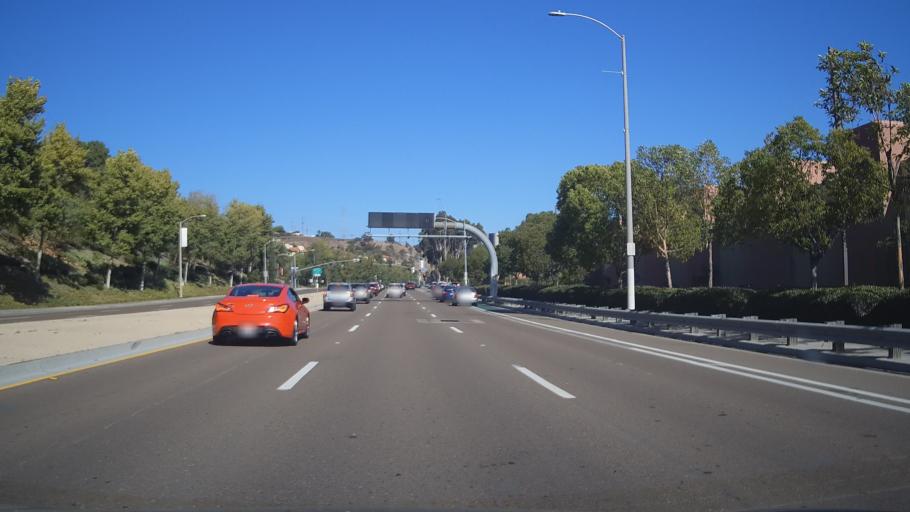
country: US
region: California
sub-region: San Diego County
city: San Diego
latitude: 32.7826
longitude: -117.1297
